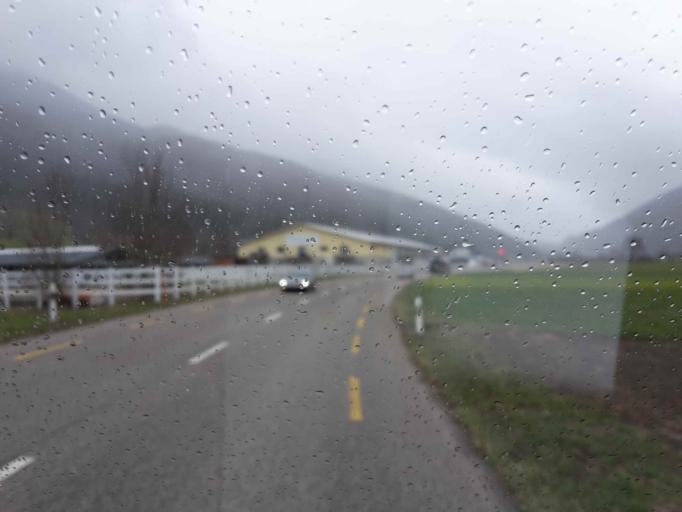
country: CH
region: Solothurn
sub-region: Bezirk Thal
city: Matzendorf
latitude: 47.2996
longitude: 7.6186
